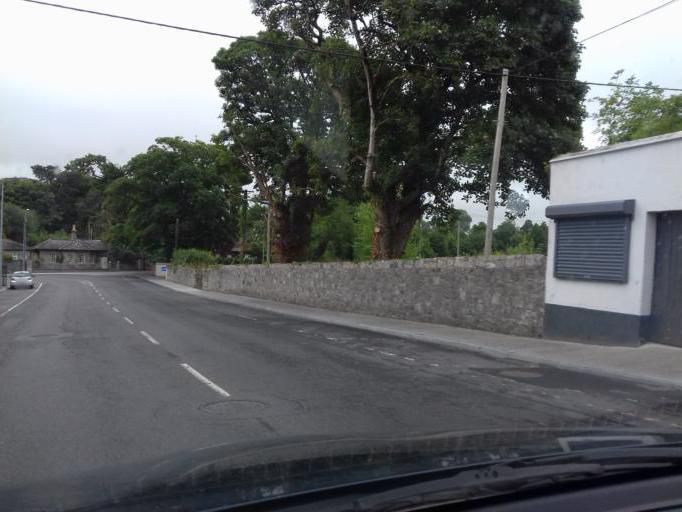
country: IE
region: Leinster
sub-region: County Carlow
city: Bagenalstown
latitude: 52.7027
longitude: -6.9559
